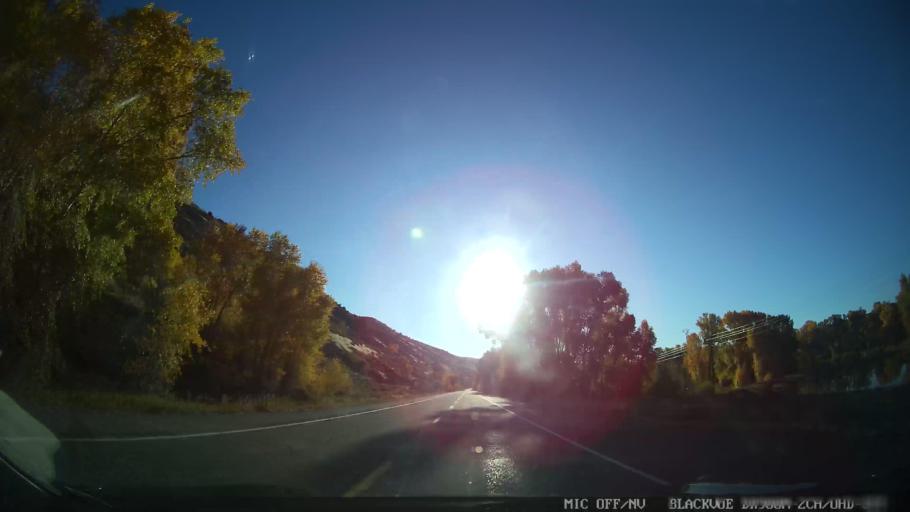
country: US
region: Colorado
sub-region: Grand County
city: Hot Sulphur Springs
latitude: 40.0650
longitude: -106.1925
